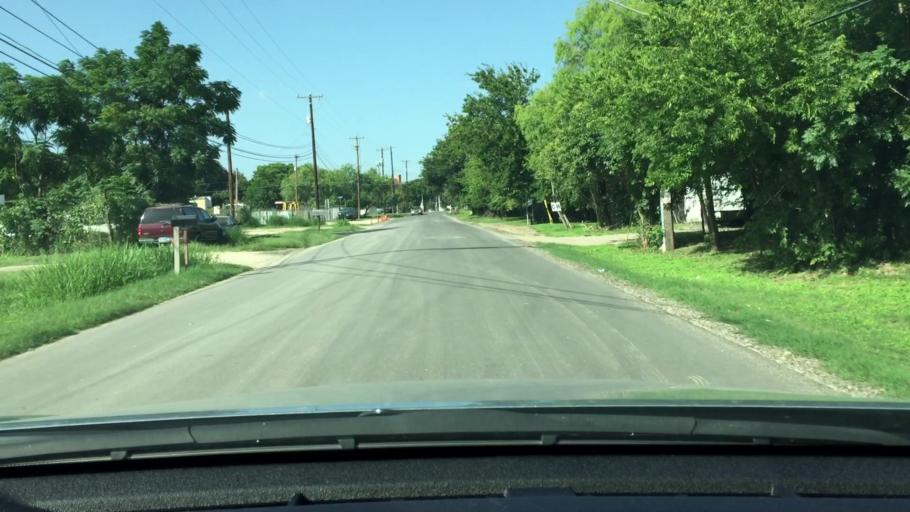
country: US
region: Texas
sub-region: Bexar County
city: Windcrest
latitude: 29.5266
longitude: -98.3894
